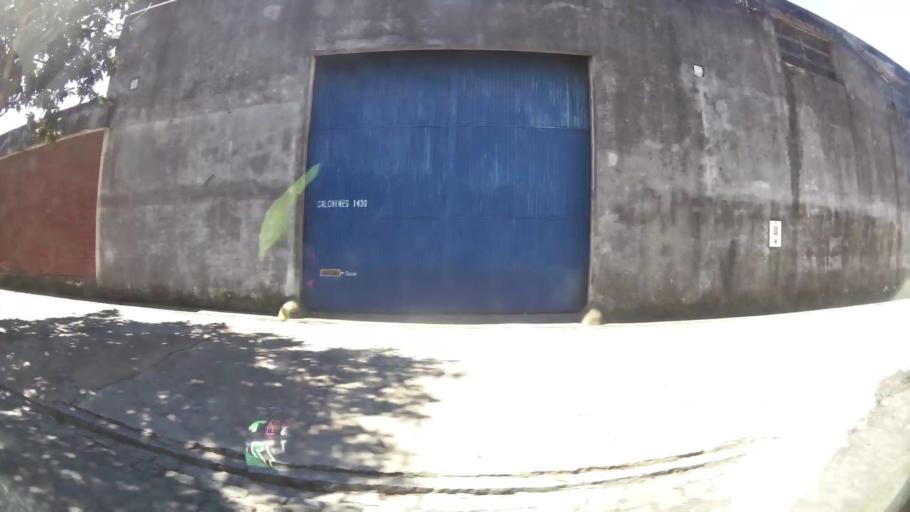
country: AR
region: Santa Fe
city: Santa Fe de la Vera Cruz
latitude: -31.6430
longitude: -60.6917
